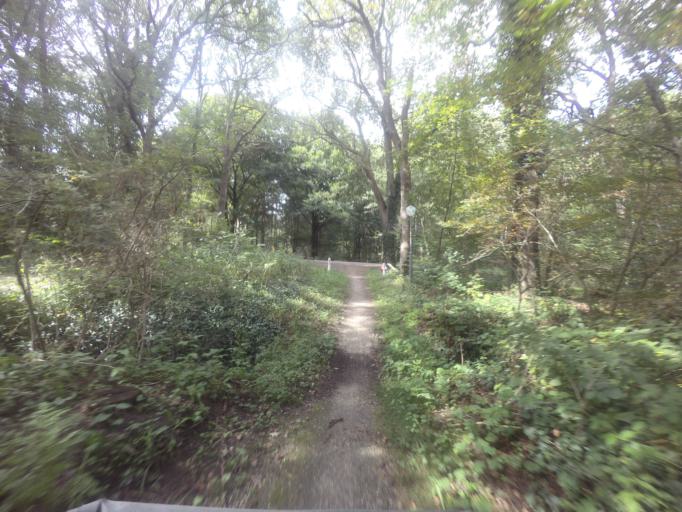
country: NL
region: Drenthe
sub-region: Gemeente Assen
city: Assen
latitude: 53.0451
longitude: 6.4414
